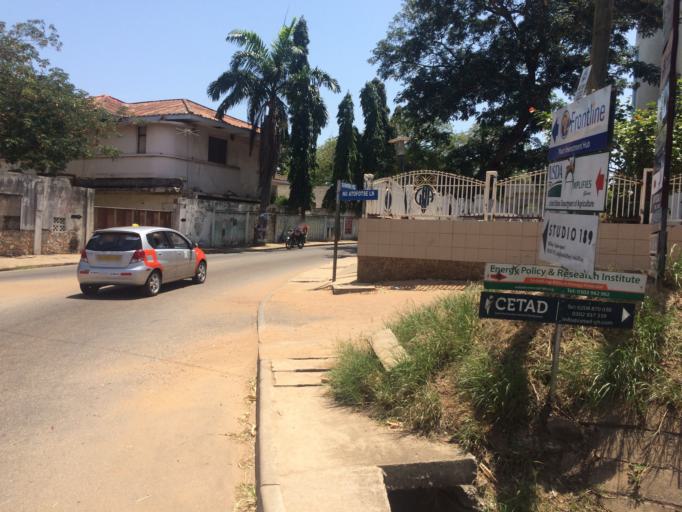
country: GH
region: Greater Accra
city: Accra
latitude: 5.5684
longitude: -0.1837
